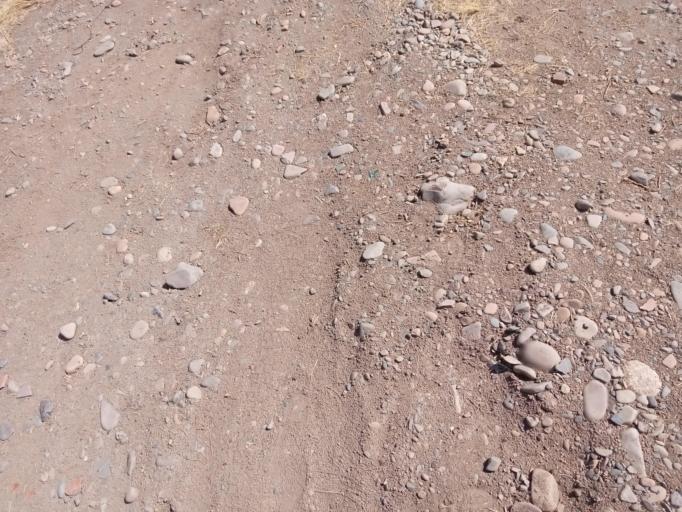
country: BO
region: La Paz
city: Batallas
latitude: -16.4397
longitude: -68.3752
